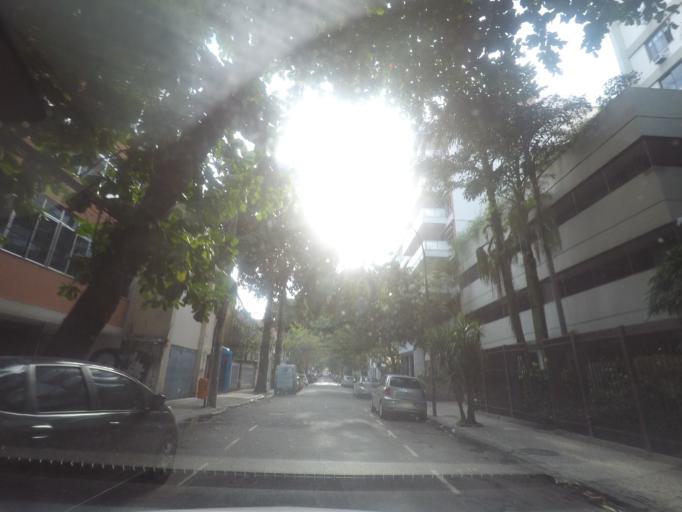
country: BR
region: Rio de Janeiro
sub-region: Rio De Janeiro
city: Rio de Janeiro
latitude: -22.9569
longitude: -43.1950
